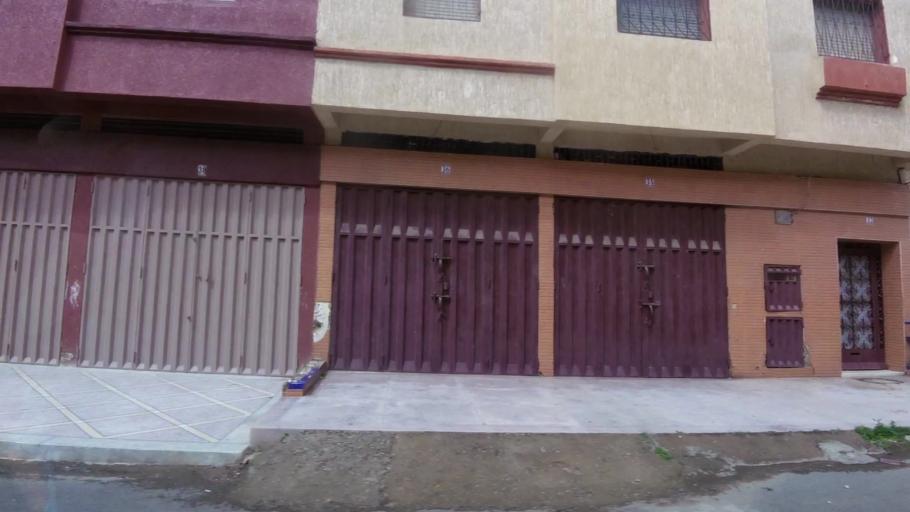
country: MA
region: Chaouia-Ouardigha
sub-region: Settat Province
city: Berrechid
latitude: 33.2730
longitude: -7.5906
